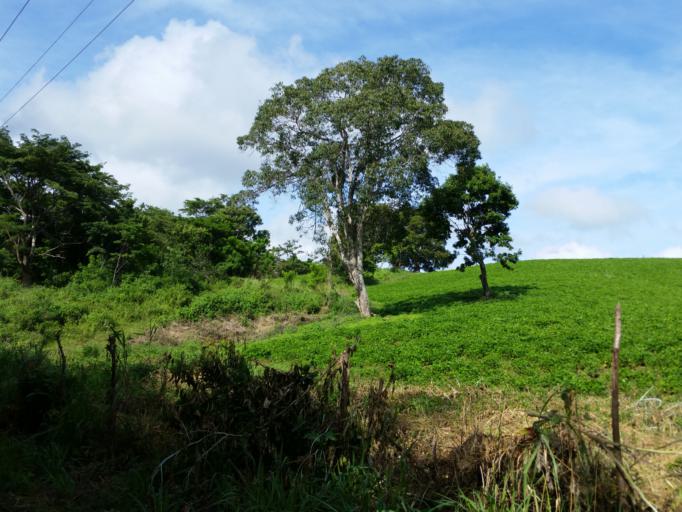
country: NI
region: Masaya
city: Ticuantepe
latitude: 12.0660
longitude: -86.2559
